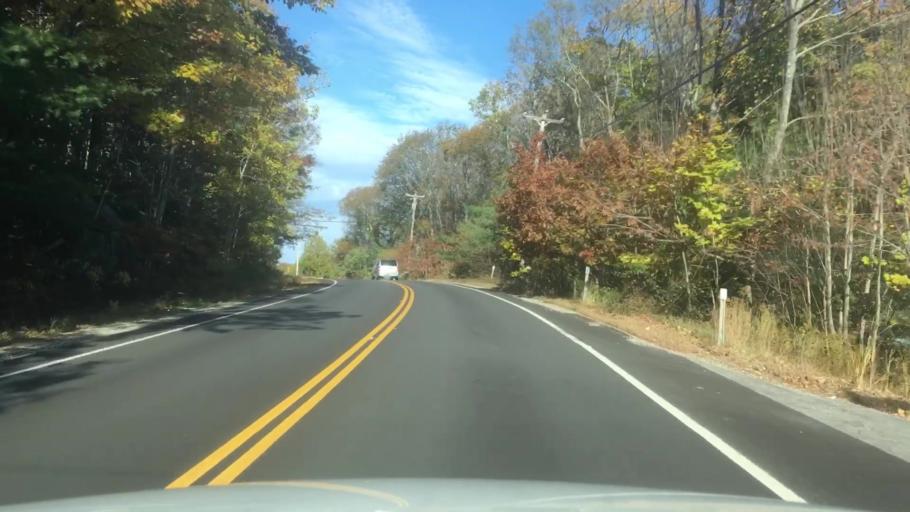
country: US
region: Maine
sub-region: Sagadahoc County
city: Woolwich
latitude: 43.9075
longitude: -69.7978
